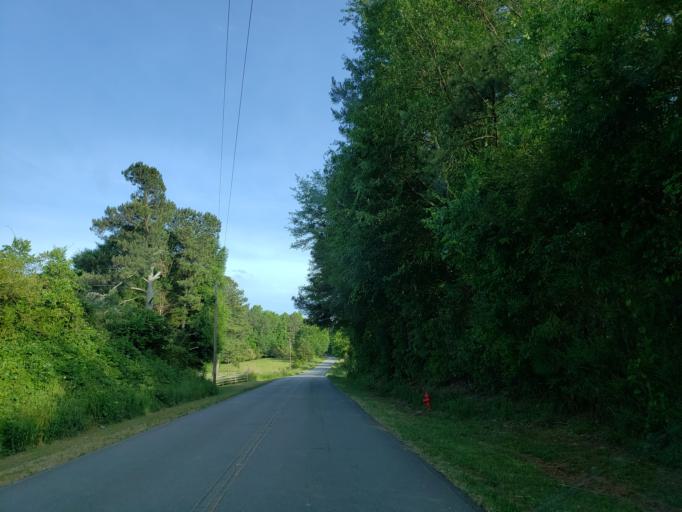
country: US
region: Georgia
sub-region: Carroll County
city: Bowdon
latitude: 33.4722
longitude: -85.2984
